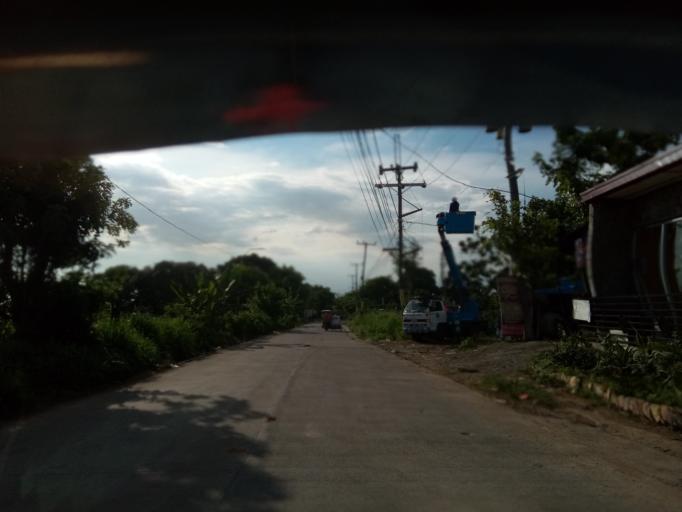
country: PH
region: Calabarzon
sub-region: Province of Cavite
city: Javalera
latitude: 14.2850
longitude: 120.9438
